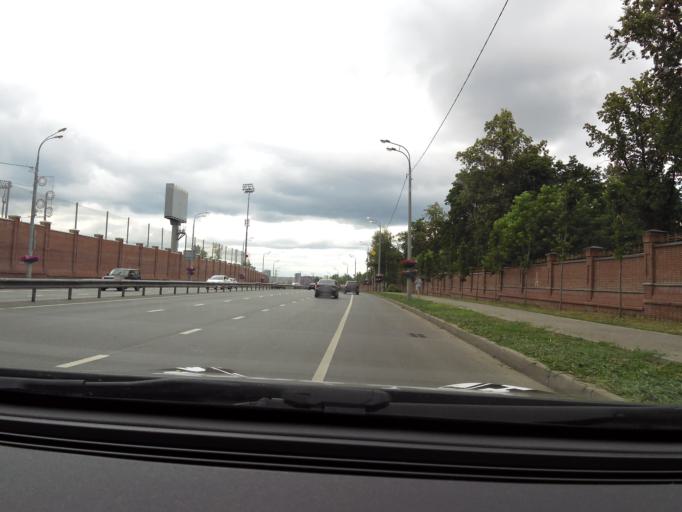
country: RU
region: Tatarstan
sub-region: Gorod Kazan'
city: Kazan
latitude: 55.7952
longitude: 49.1551
